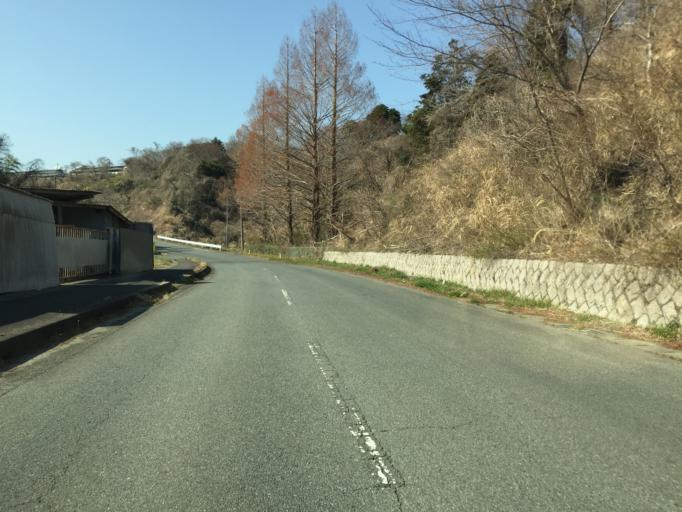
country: JP
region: Fukushima
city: Iwaki
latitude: 36.9702
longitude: 140.9309
